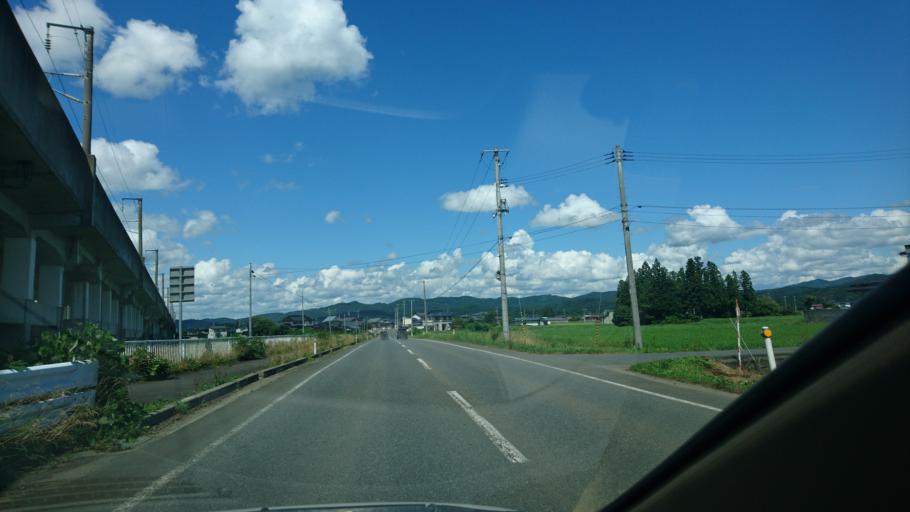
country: JP
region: Iwate
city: Kitakami
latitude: 39.3032
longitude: 141.1361
